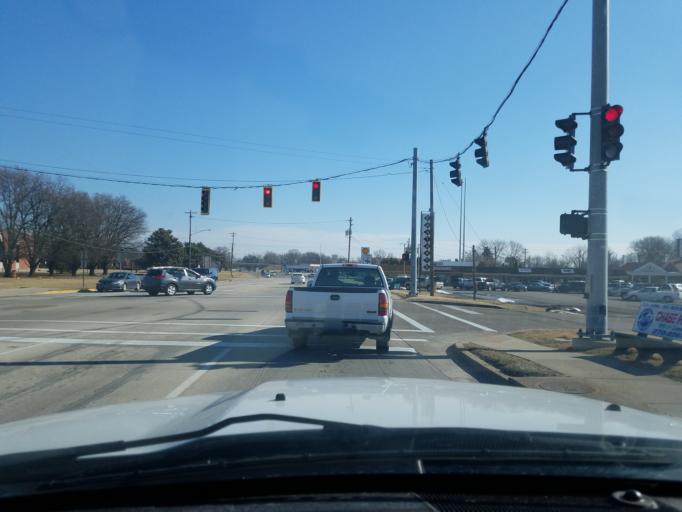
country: US
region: Kentucky
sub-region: Henderson County
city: Henderson
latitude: 37.8325
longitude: -87.5718
